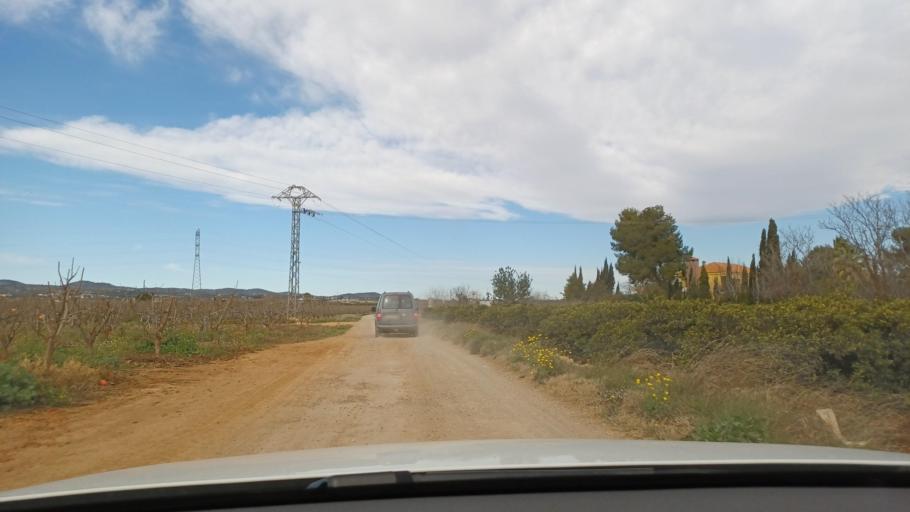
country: ES
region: Valencia
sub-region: Provincia de Valencia
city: Benifaio
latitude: 39.2910
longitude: -0.4421
